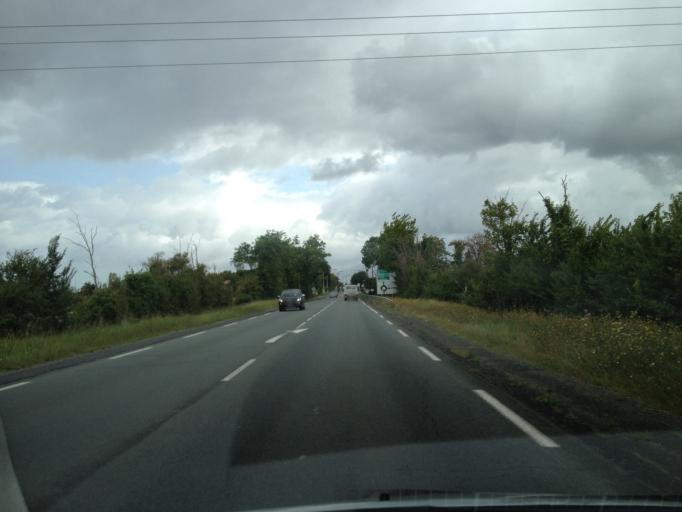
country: FR
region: Poitou-Charentes
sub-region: Departement de la Charente-Maritime
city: Marans
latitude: 46.2929
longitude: -0.9919
